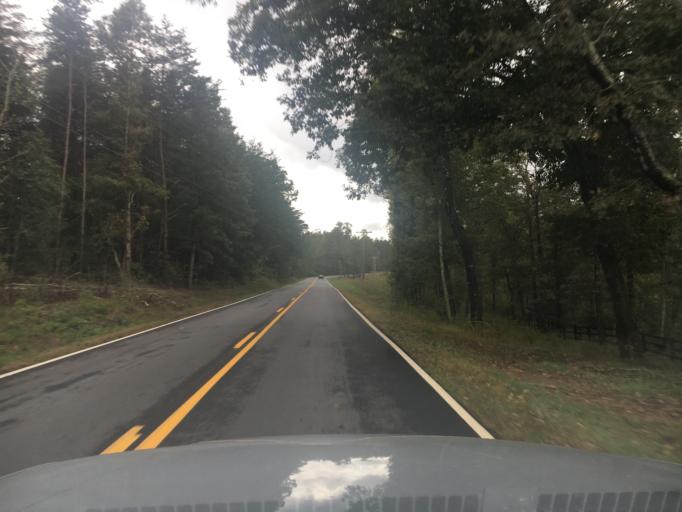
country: US
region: North Carolina
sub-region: Polk County
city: Columbus
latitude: 35.2664
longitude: -82.0587
